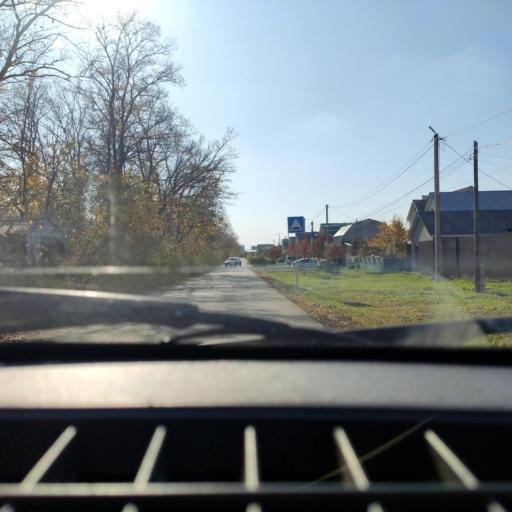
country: RU
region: Bashkortostan
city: Ufa
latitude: 54.6261
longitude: 55.9137
